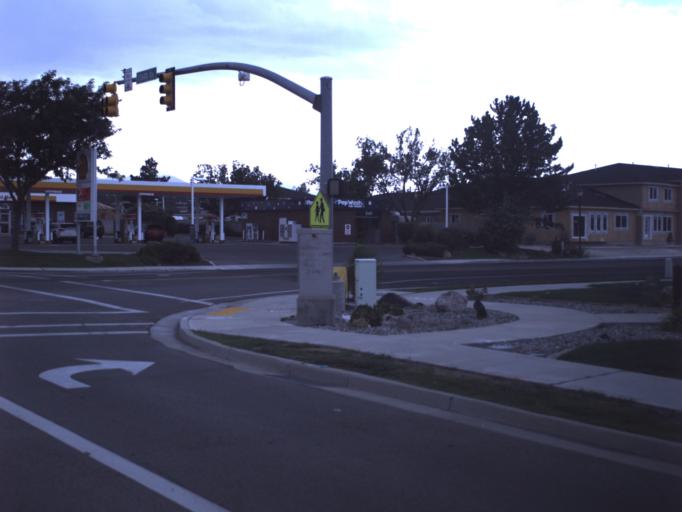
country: US
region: Utah
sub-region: Salt Lake County
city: Riverton
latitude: 40.5224
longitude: -111.9288
